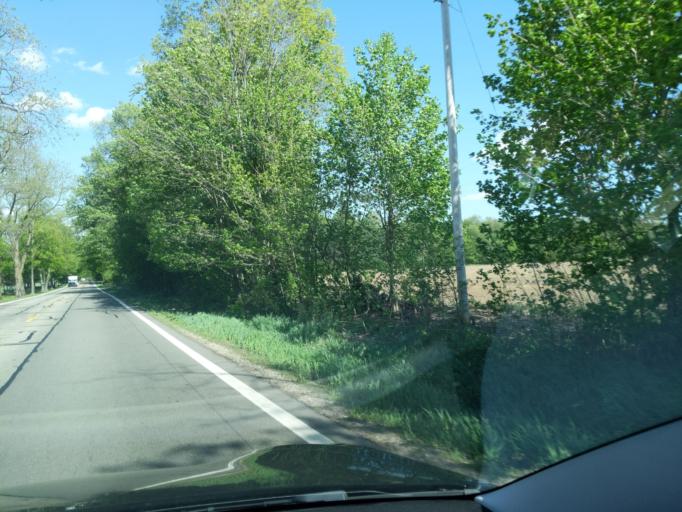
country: US
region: Michigan
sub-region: Barry County
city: Middleville
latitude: 42.7983
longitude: -85.3644
